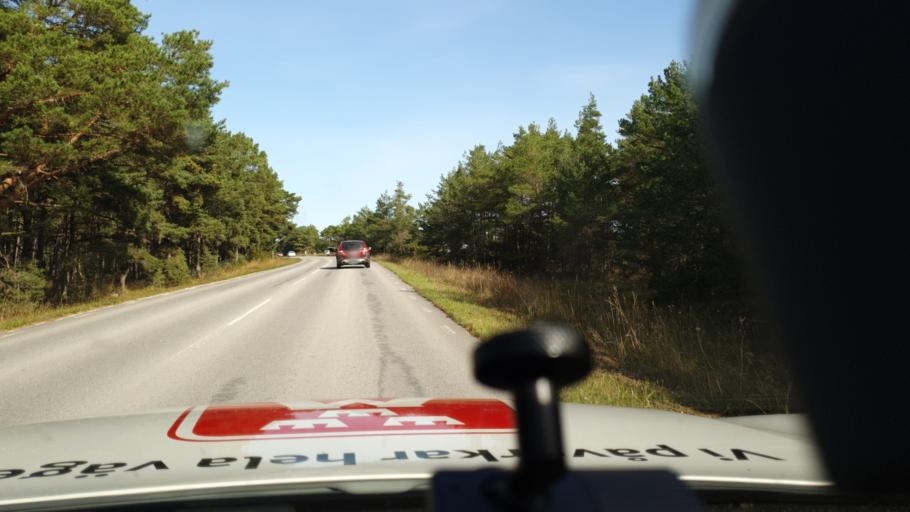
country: SE
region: Gotland
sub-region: Gotland
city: Slite
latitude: 57.8769
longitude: 19.0860
